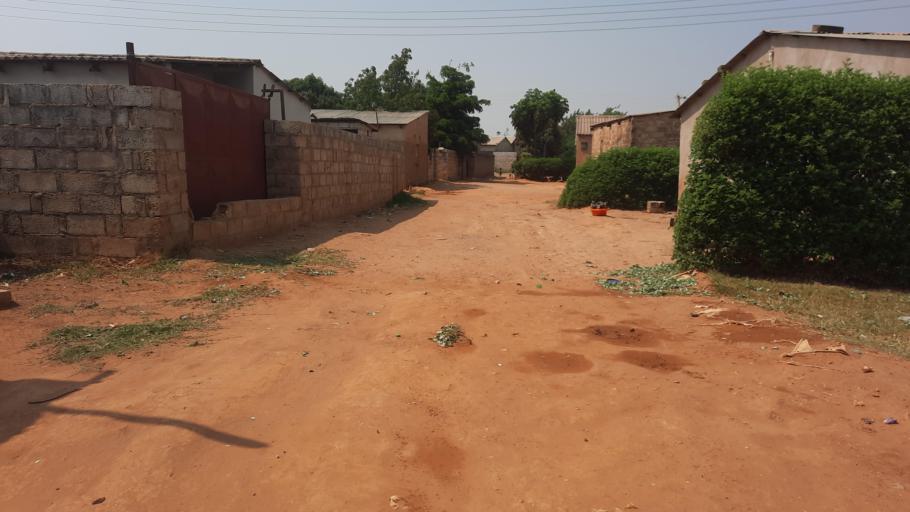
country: ZM
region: Lusaka
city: Lusaka
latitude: -15.3926
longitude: 28.3832
